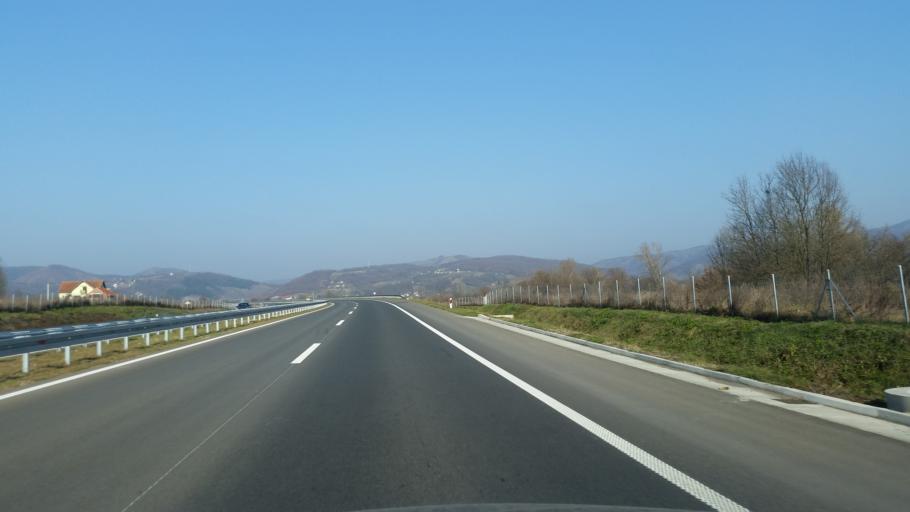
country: RS
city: Prislonica
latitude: 43.9488
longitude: 20.4007
